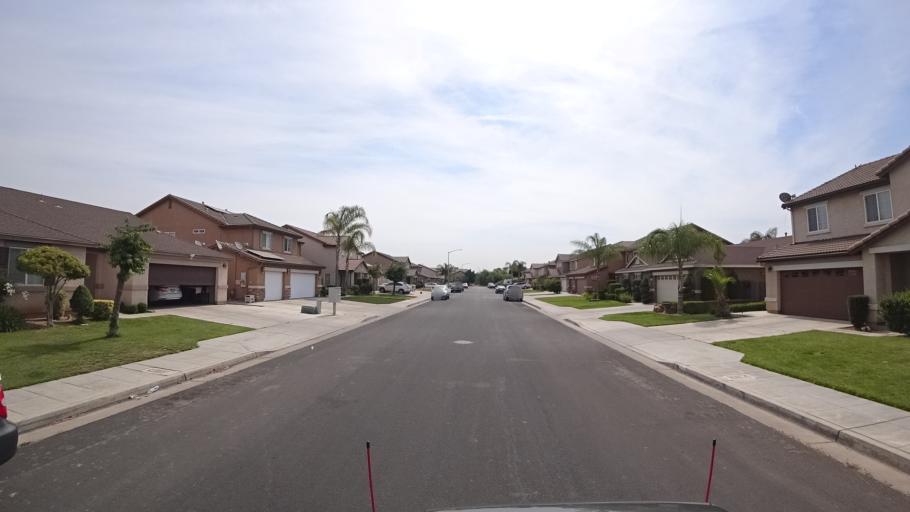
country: US
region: California
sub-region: Fresno County
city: West Park
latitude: 36.7619
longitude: -119.8871
